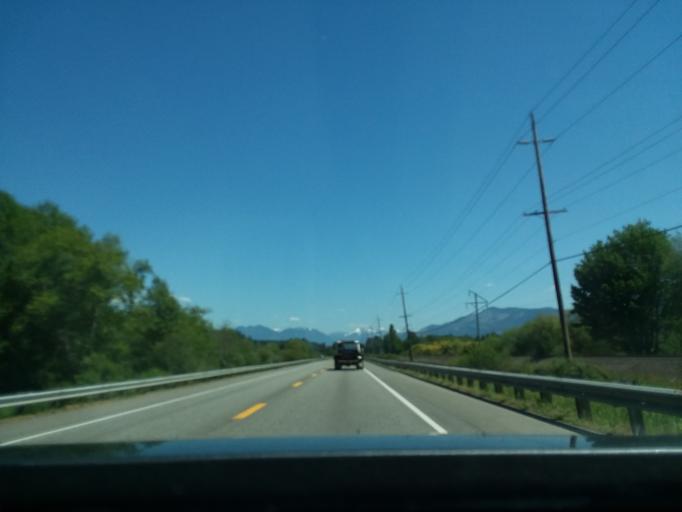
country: US
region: Washington
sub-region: Snohomish County
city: Monroe
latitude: 47.8566
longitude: -121.9422
